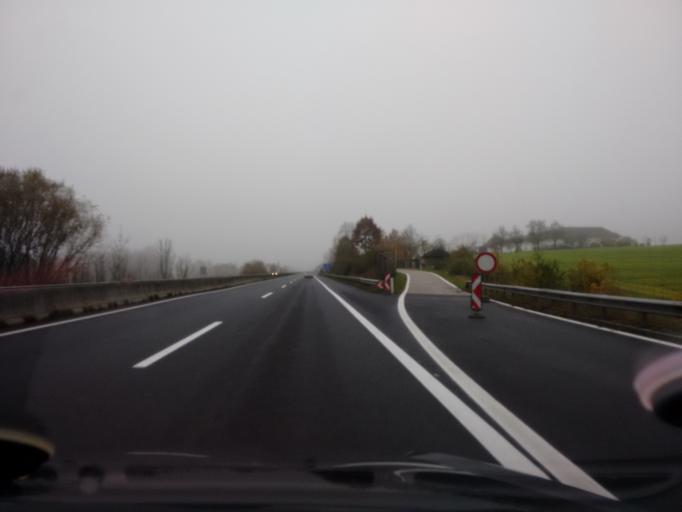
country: AT
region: Upper Austria
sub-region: Wels-Land
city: Sattledt
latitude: 48.0307
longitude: 14.0628
